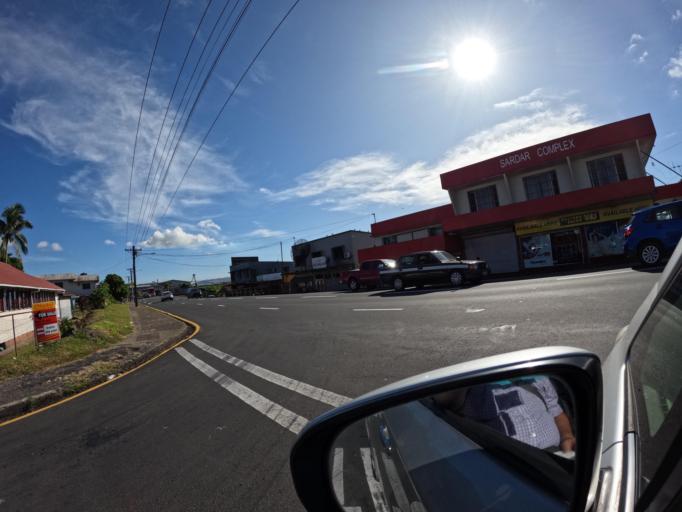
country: FJ
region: Central
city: Suva
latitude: -18.1439
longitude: 178.4481
